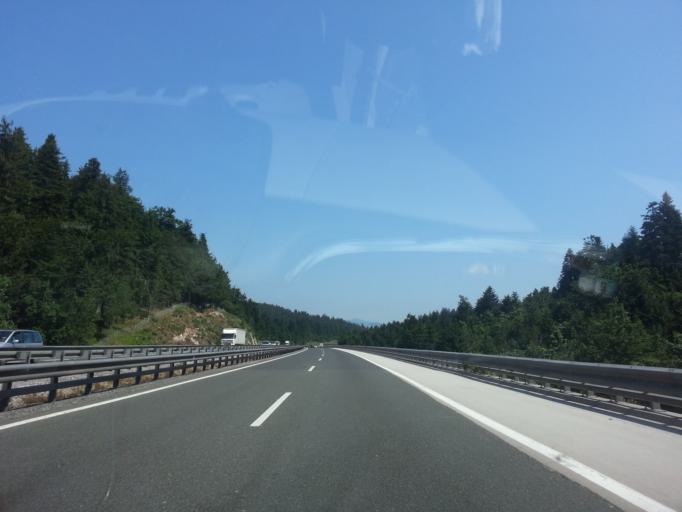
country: SI
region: Vrhnika
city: Vrhnika
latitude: 45.9272
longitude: 14.2699
